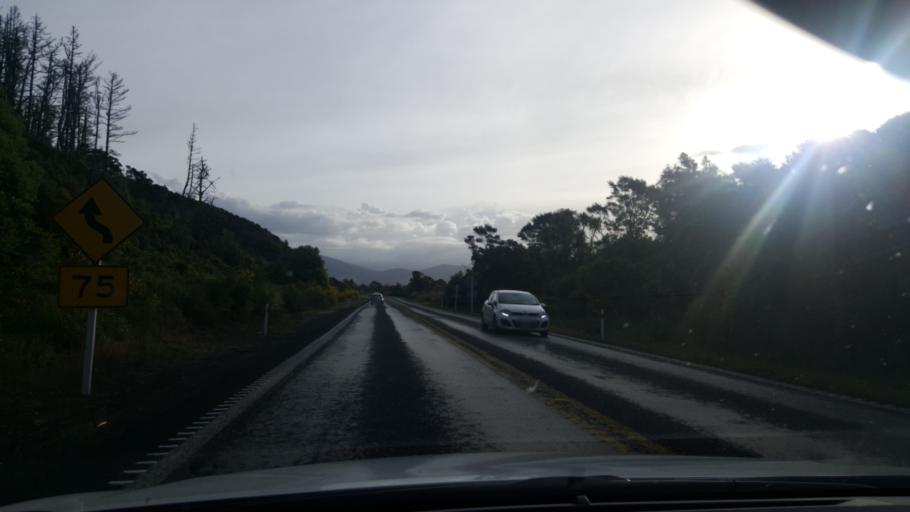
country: NZ
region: Waikato
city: Turangi
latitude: -38.9382
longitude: 175.8605
